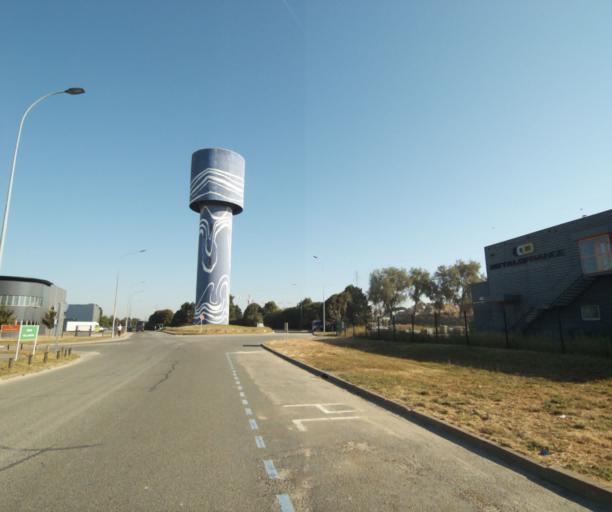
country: FR
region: Ile-de-France
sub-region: Departement de Seine-et-Marne
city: Lieusaint
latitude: 48.6177
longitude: 2.5717
